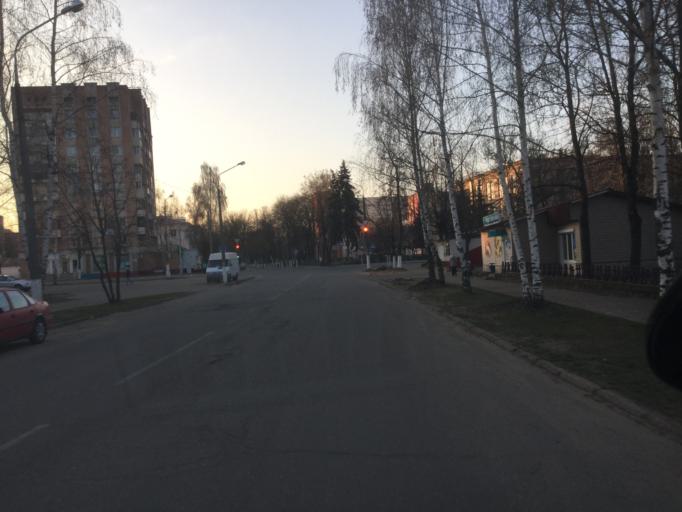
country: BY
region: Vitebsk
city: Vitebsk
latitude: 55.1668
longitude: 30.1302
